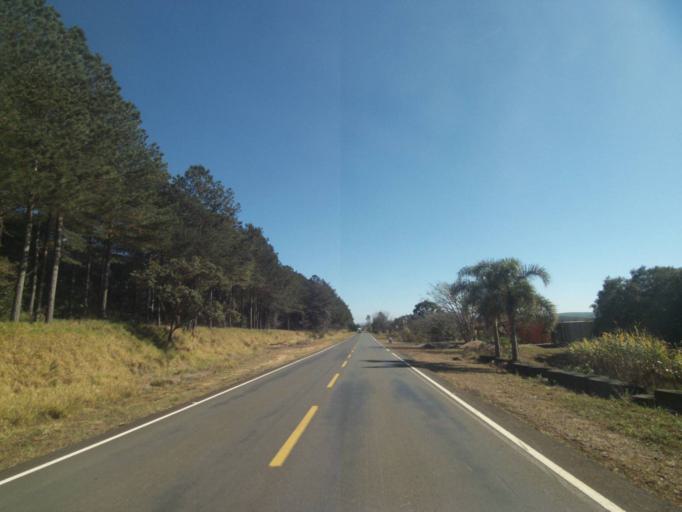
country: BR
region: Parana
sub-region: Telemaco Borba
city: Telemaco Borba
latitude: -24.4347
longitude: -50.5544
